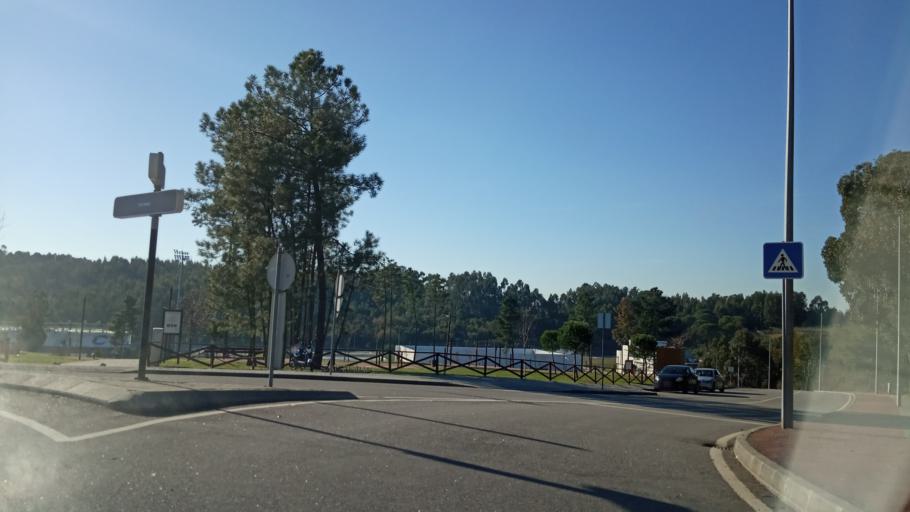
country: PT
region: Aveiro
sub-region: Anadia
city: Anadia
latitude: 40.4292
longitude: -8.4373
